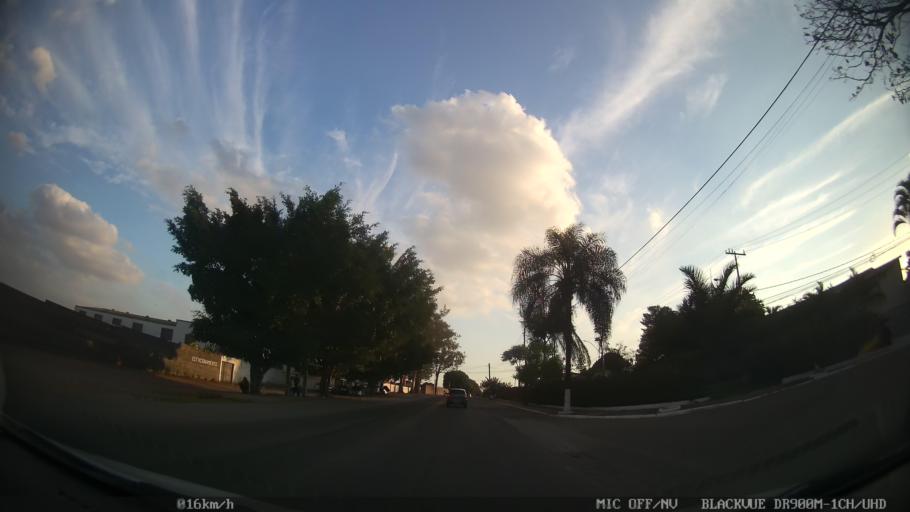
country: BR
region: Sao Paulo
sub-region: Hortolandia
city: Hortolandia
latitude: -22.8827
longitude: -47.1564
